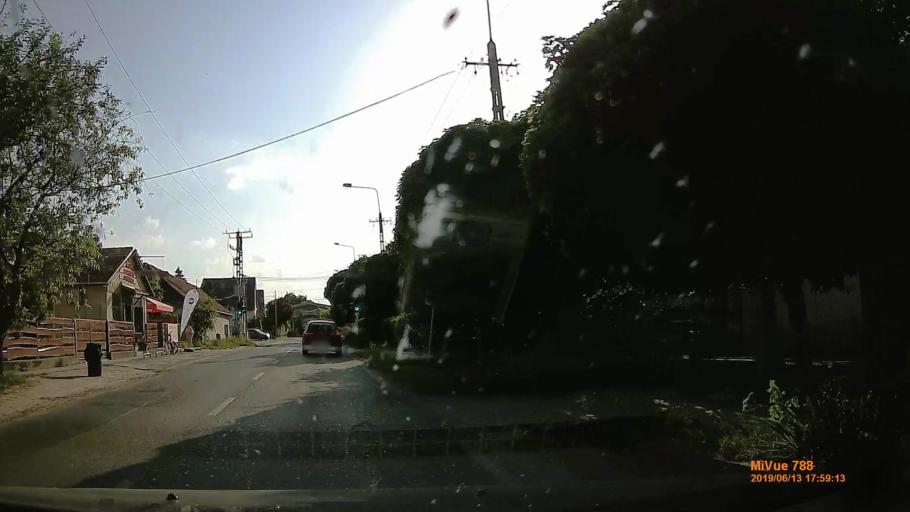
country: HU
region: Pest
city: Ecser
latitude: 47.4447
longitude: 19.3161
